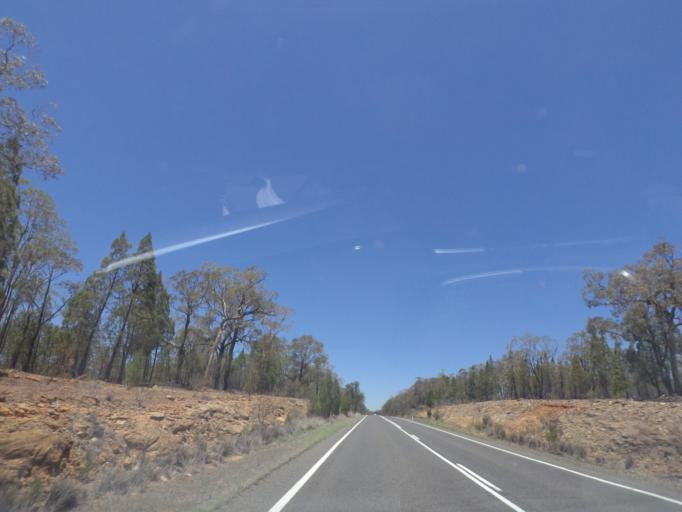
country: AU
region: New South Wales
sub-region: Narrabri
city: Narrabri
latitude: -30.7026
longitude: 149.5338
